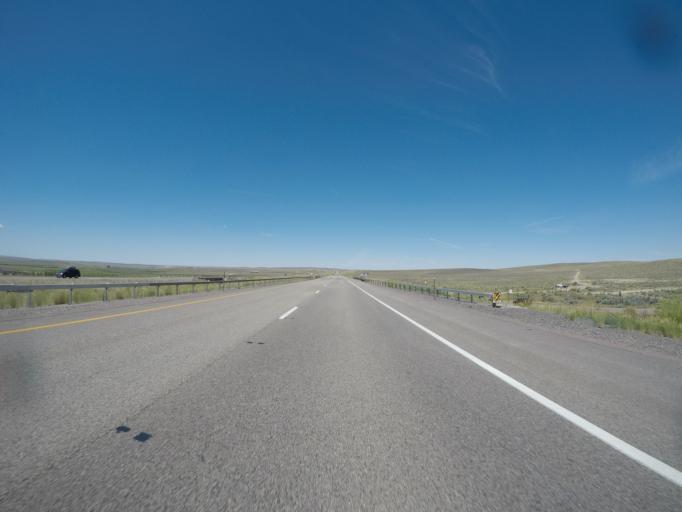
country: US
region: Wyoming
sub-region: Carbon County
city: Saratoga
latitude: 41.7433
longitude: -106.7728
